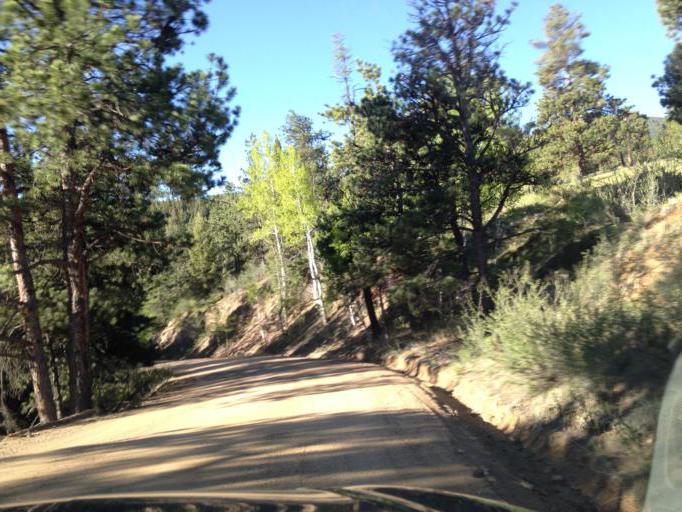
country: US
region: Colorado
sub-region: Jefferson County
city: Evergreen
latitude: 39.4054
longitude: -105.5182
